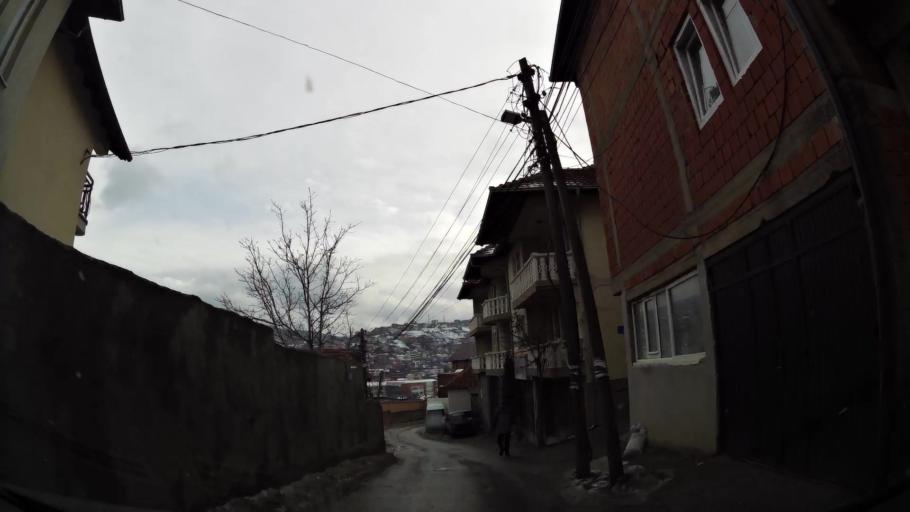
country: XK
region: Pristina
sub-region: Komuna e Prishtines
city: Pristina
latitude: 42.6806
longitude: 21.1710
